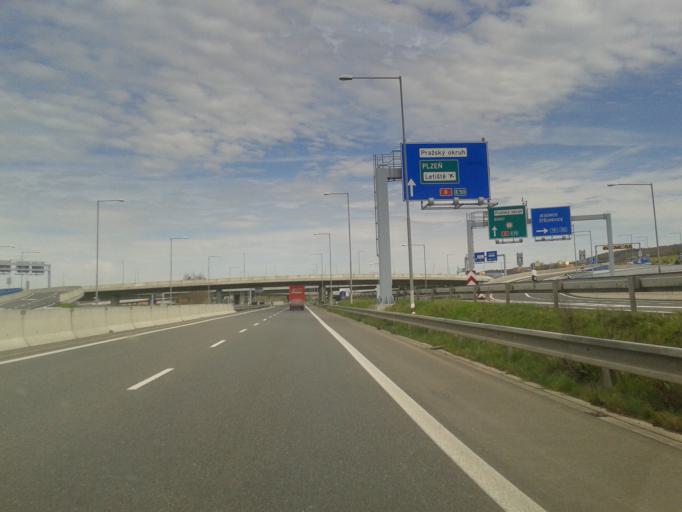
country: CZ
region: Praha
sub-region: Praha 12
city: Modrany
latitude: 49.9828
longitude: 14.3915
